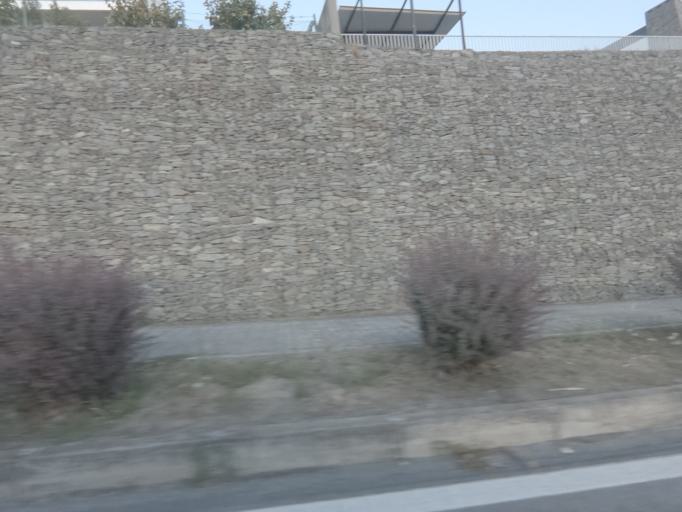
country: PT
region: Vila Real
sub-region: Peso da Regua
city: Peso da Regua
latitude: 41.1597
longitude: -7.7805
